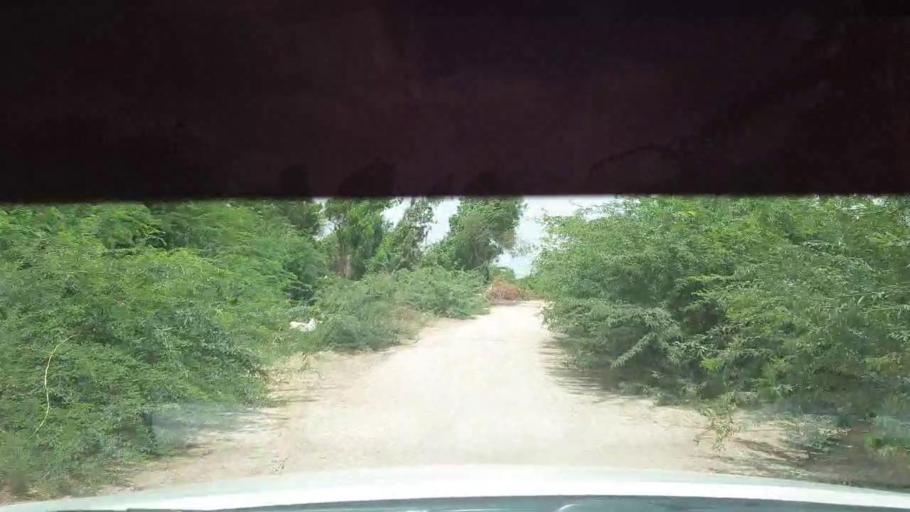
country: PK
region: Sindh
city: Kadhan
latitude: 24.4647
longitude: 69.0354
